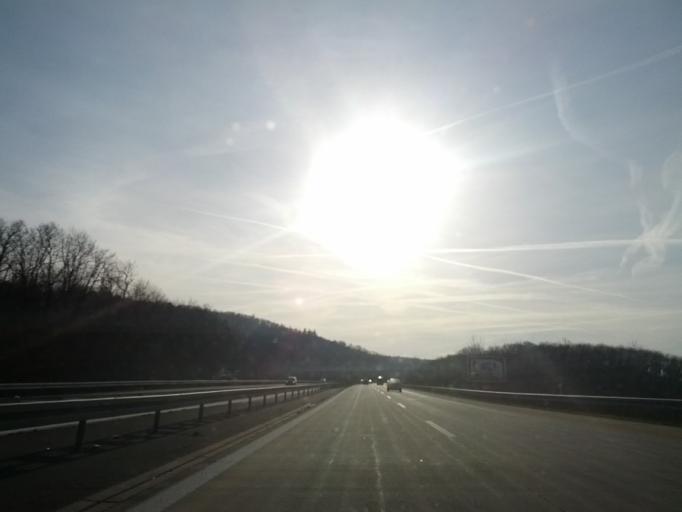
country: DE
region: Bavaria
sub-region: Regierungsbezirk Mittelfranken
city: Steinsfeld
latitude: 49.4079
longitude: 10.2456
